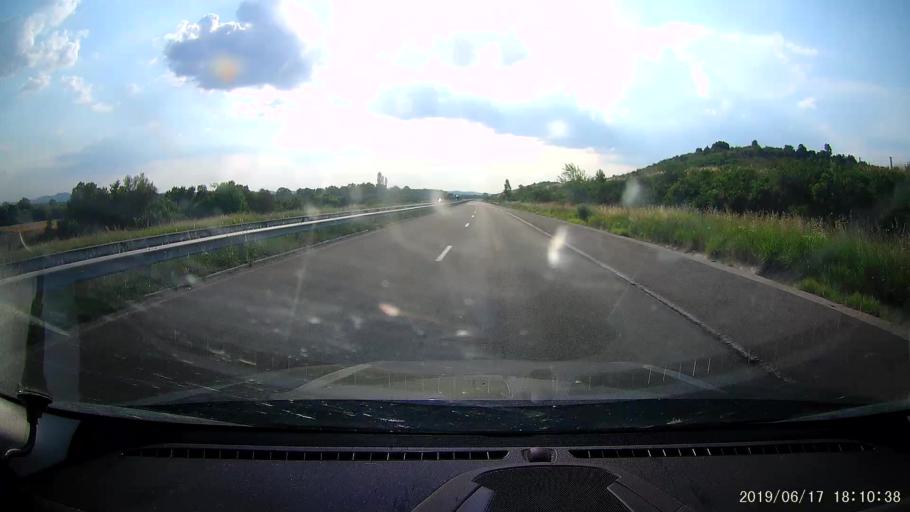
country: BG
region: Khaskovo
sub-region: Obshtina Lyubimets
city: Lyubimets
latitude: 41.8762
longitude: 26.0724
